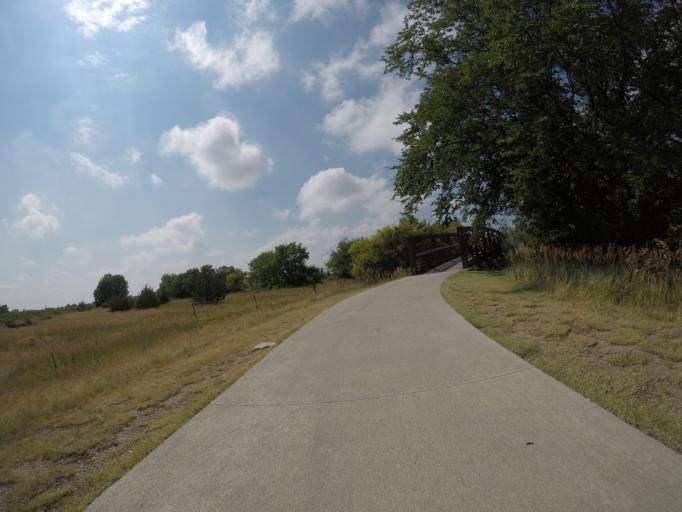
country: US
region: Nebraska
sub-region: Buffalo County
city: Kearney
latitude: 40.6769
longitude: -99.1045
